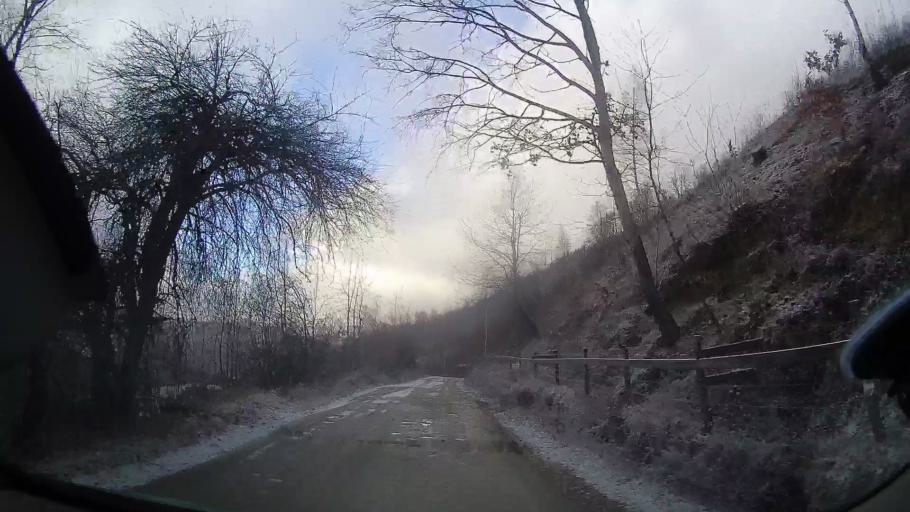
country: RO
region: Cluj
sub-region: Comuna Valea Ierii
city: Valea Ierii
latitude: 46.6704
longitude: 23.3275
